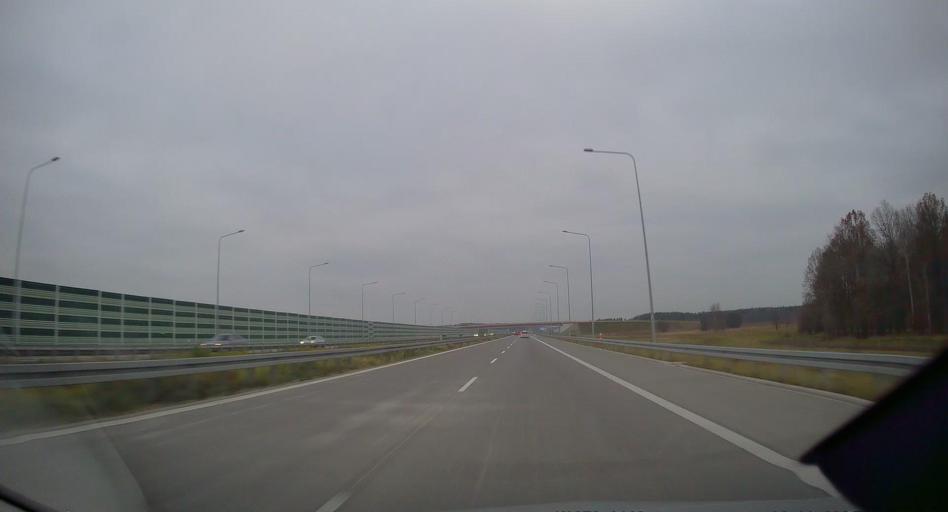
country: PL
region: Silesian Voivodeship
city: Wozniki
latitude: 50.5837
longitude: 19.0447
